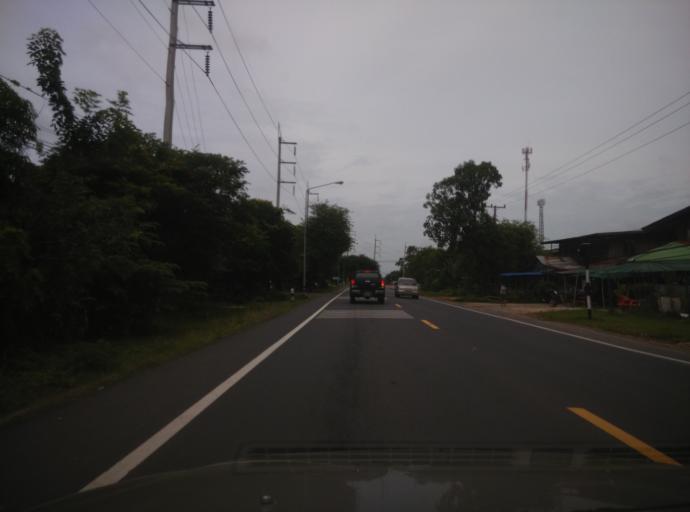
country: TH
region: Sisaket
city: Uthumphon Phisai
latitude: 15.0752
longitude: 104.1009
